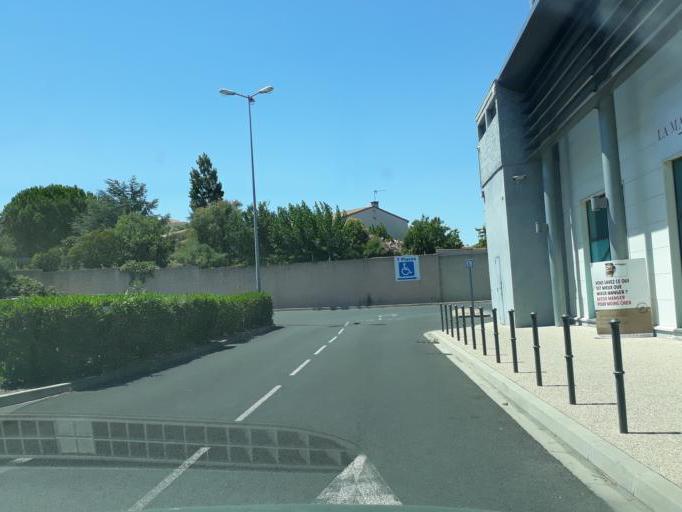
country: FR
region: Languedoc-Roussillon
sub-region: Departement de l'Herault
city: Agde
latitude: 43.3071
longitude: 3.4904
